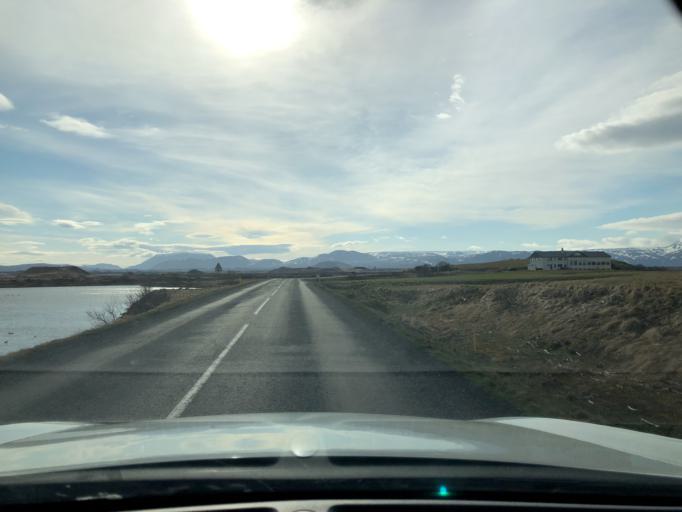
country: IS
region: Northeast
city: Laugar
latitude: 65.5668
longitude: -17.0316
